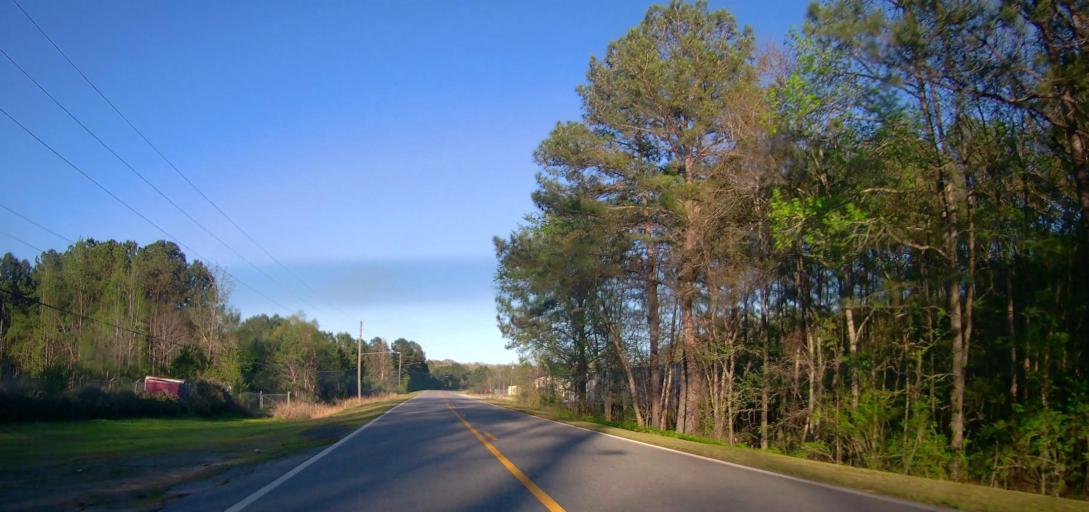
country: US
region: Georgia
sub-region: Wilkinson County
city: Irwinton
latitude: 32.8480
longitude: -83.1981
